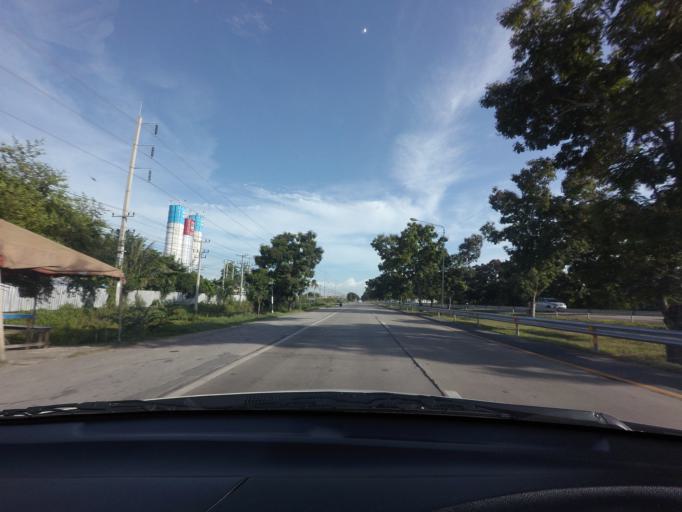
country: TH
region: Phra Nakhon Si Ayutthaya
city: Lat Bua Luang
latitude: 14.1840
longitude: 100.2922
